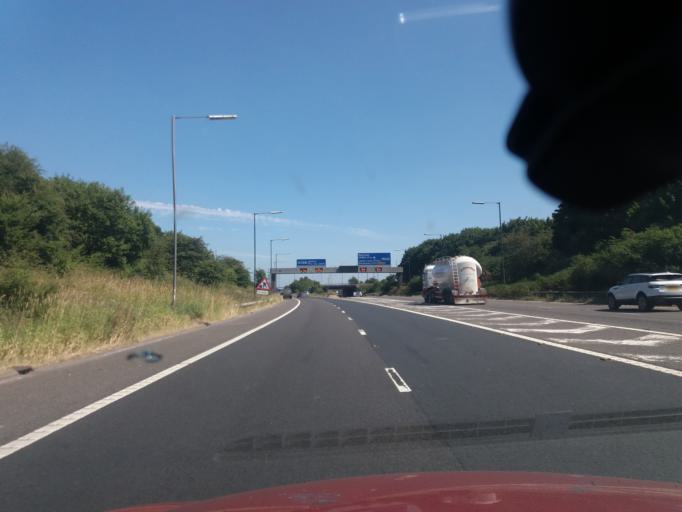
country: GB
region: England
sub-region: Borough of Bolton
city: Kearsley
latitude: 53.5335
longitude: -2.3855
